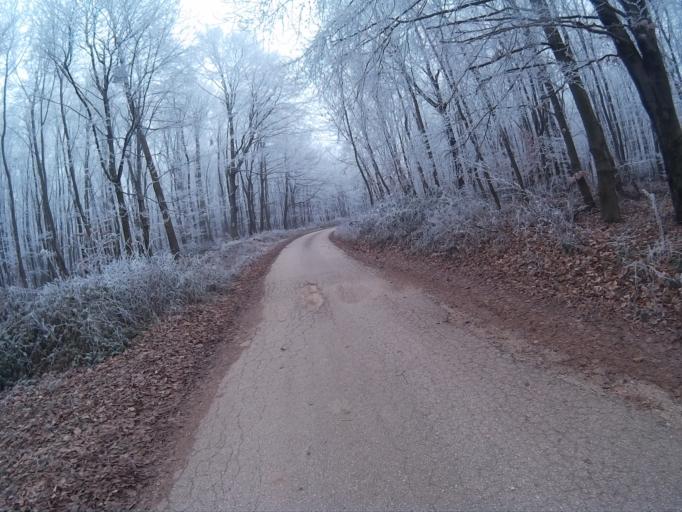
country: HU
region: Fejer
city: Pusztavam
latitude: 47.3976
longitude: 18.3061
